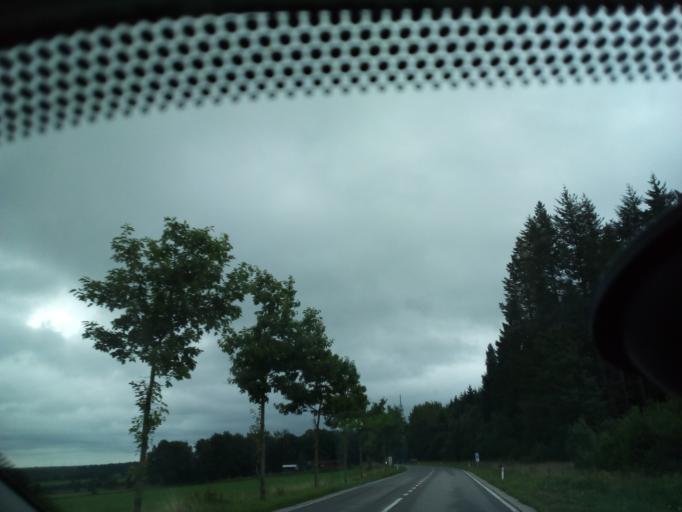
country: BE
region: Wallonia
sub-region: Province de Liege
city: Butgenbach
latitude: 50.4671
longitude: 6.1633
